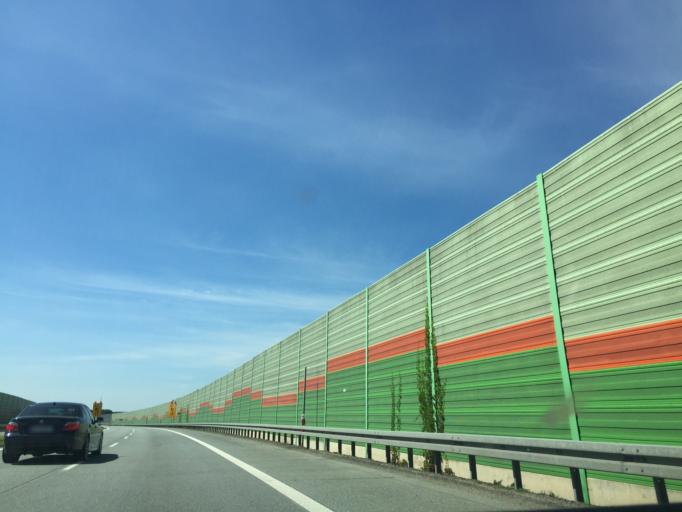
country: PL
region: Lodz Voivodeship
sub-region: Powiat tomaszowski
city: Lubochnia
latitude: 51.6086
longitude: 20.0642
